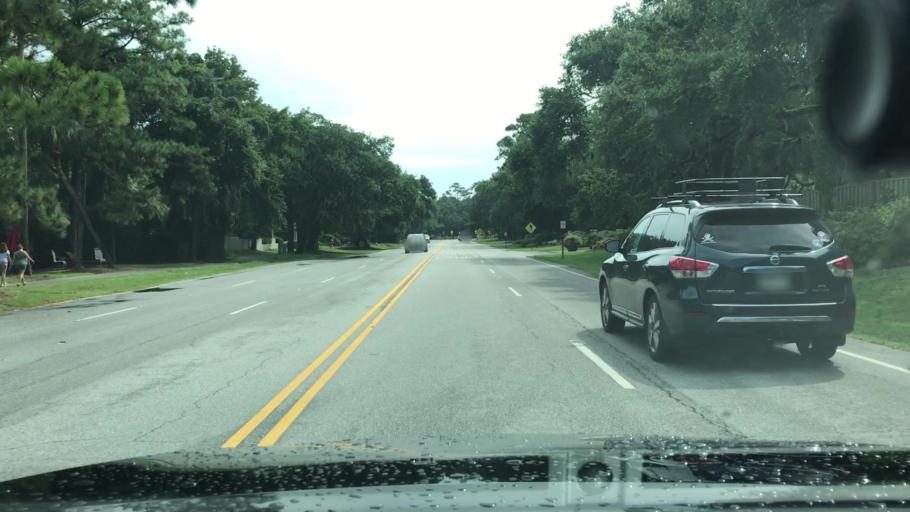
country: US
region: South Carolina
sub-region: Beaufort County
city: Hilton Head Island
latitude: 32.1409
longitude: -80.7552
